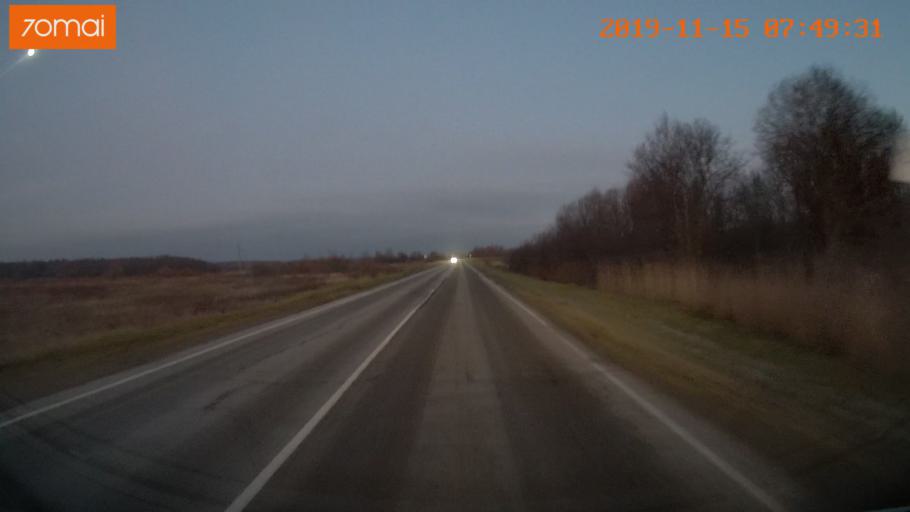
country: RU
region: Vologda
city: Cherepovets
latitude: 58.8602
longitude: 38.2312
